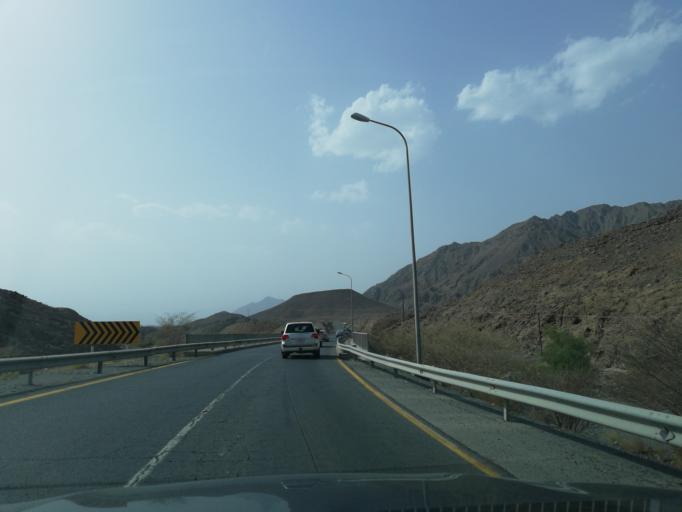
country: OM
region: Muhafazat ad Dakhiliyah
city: Sufalat Sama'il
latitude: 23.1812
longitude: 58.0981
